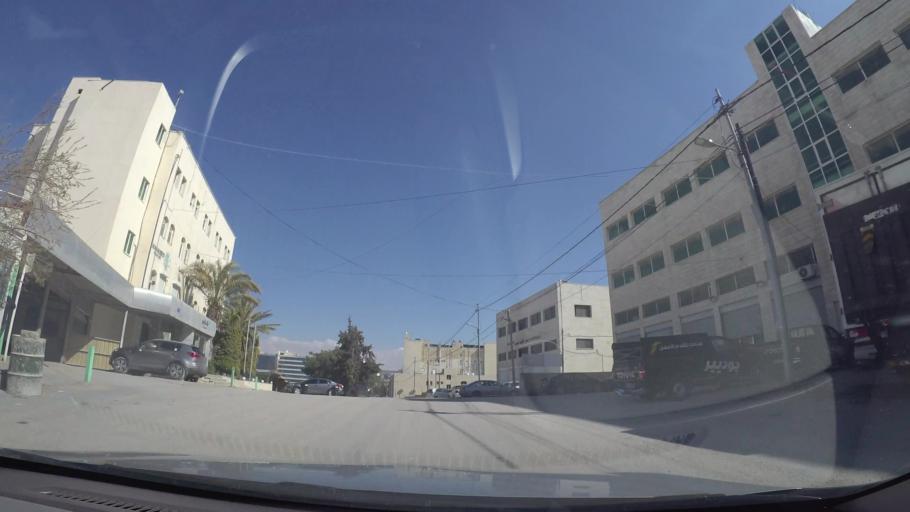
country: JO
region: Amman
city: Al Bunayyat ash Shamaliyah
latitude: 31.9122
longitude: 35.9116
